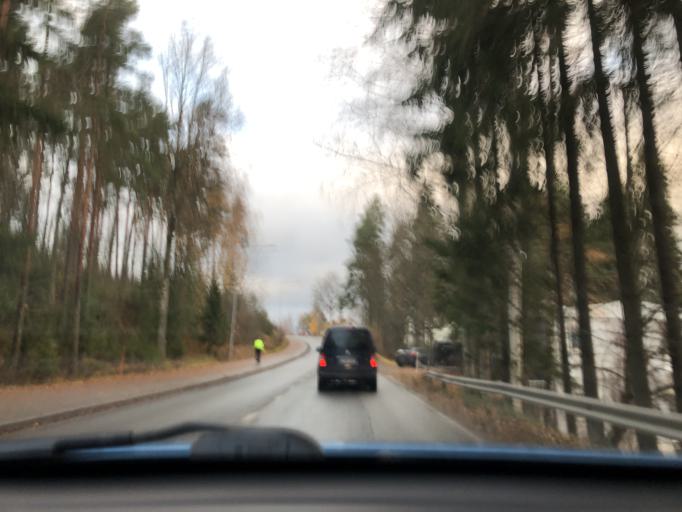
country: FI
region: Pirkanmaa
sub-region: Tampere
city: Kangasala
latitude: 61.4662
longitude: 24.0669
